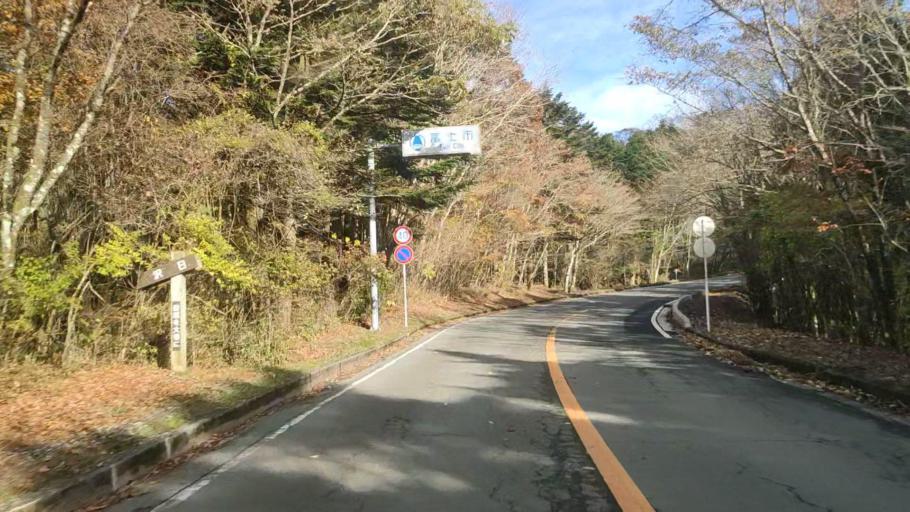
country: JP
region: Shizuoka
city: Fujinomiya
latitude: 35.3029
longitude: 138.7293
